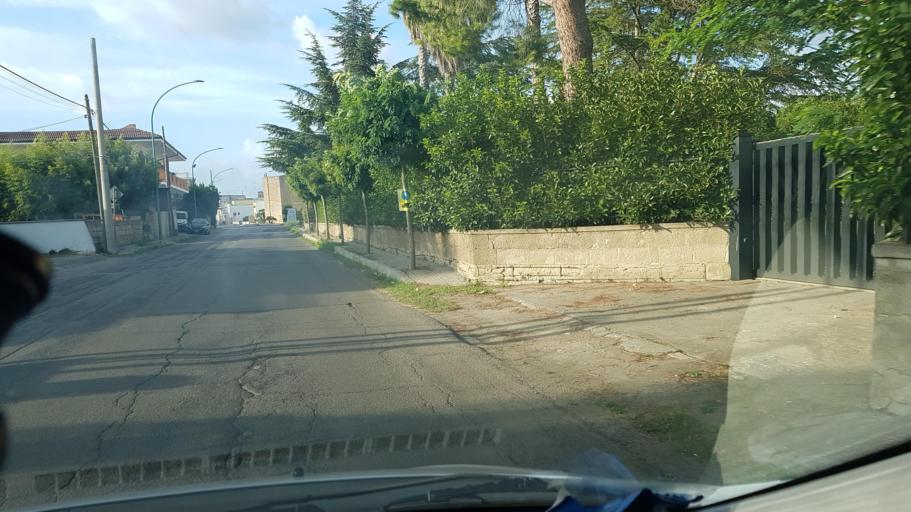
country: IT
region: Apulia
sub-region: Provincia di Lecce
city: Veglie
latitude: 40.3294
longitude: 17.9739
